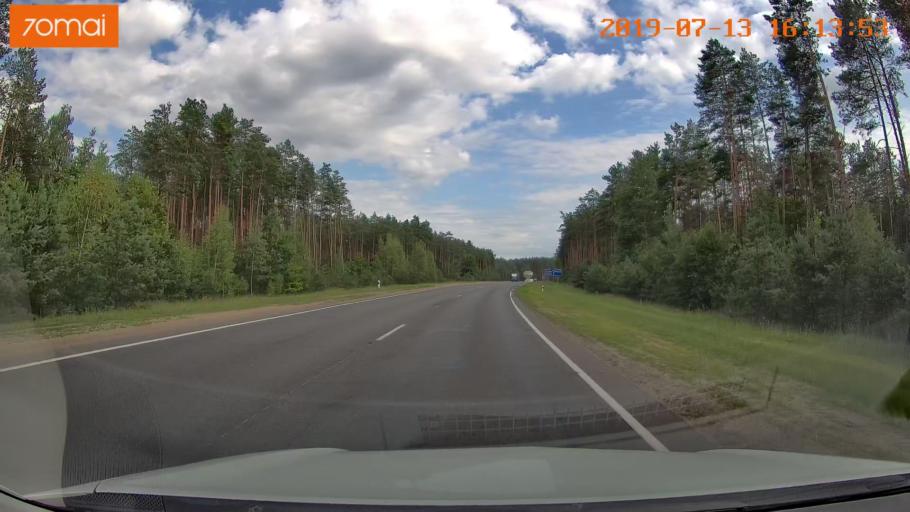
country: BY
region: Mogilev
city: Babruysk
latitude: 53.1598
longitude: 29.3127
